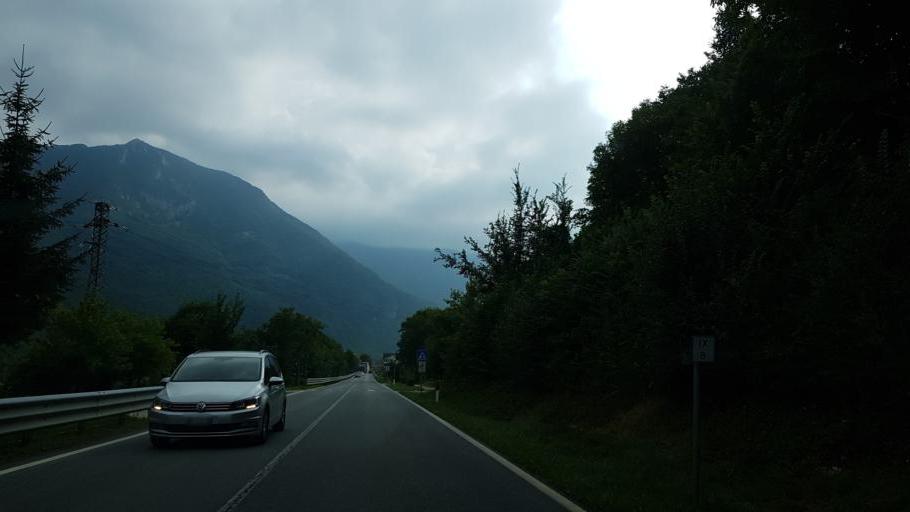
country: IT
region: Piedmont
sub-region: Provincia di Cuneo
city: Moiola
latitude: 44.3231
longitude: 7.3927
